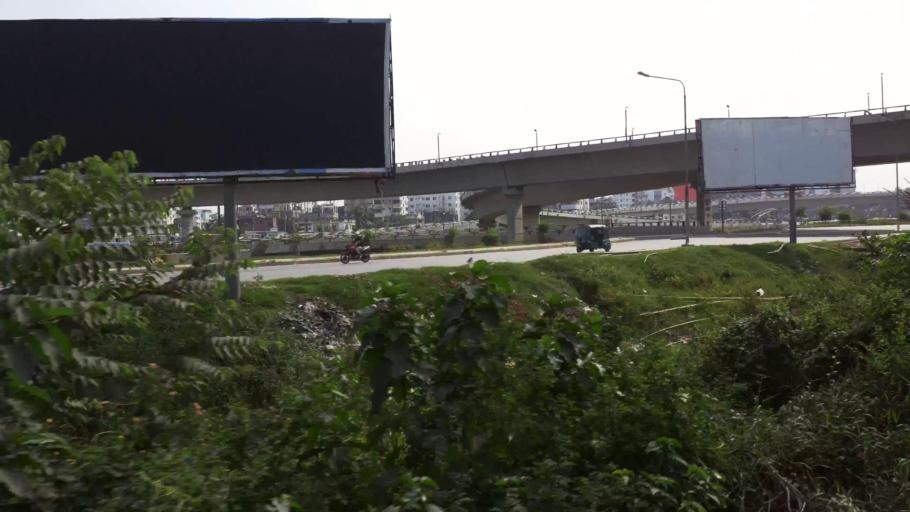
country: BD
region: Dhaka
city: Tungi
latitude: 23.8797
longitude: 90.4061
